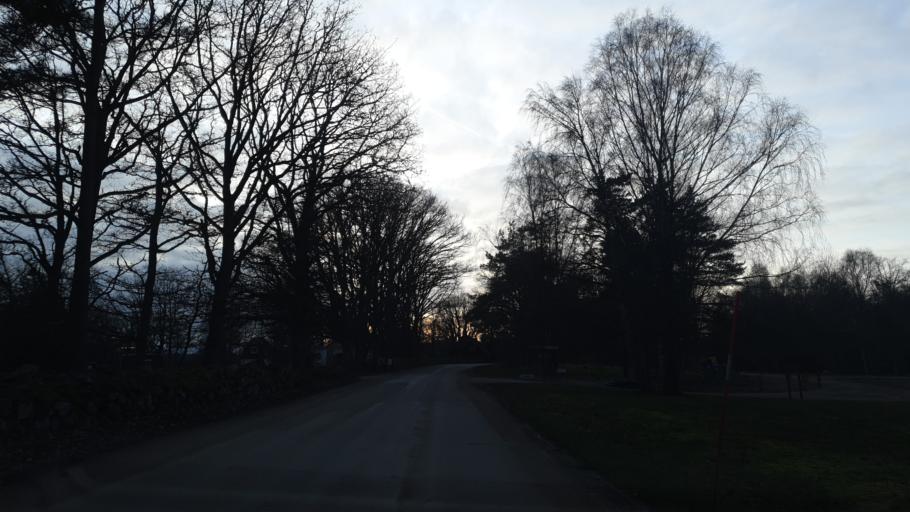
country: SE
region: Blekinge
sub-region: Karlskrona Kommun
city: Jaemjoe
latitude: 56.1596
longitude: 15.9138
